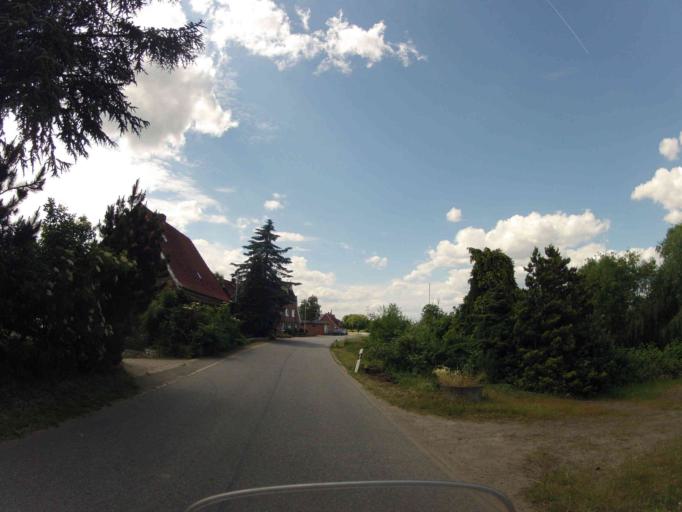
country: DE
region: Lower Saxony
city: Stelle
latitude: 53.4614
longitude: 10.1306
